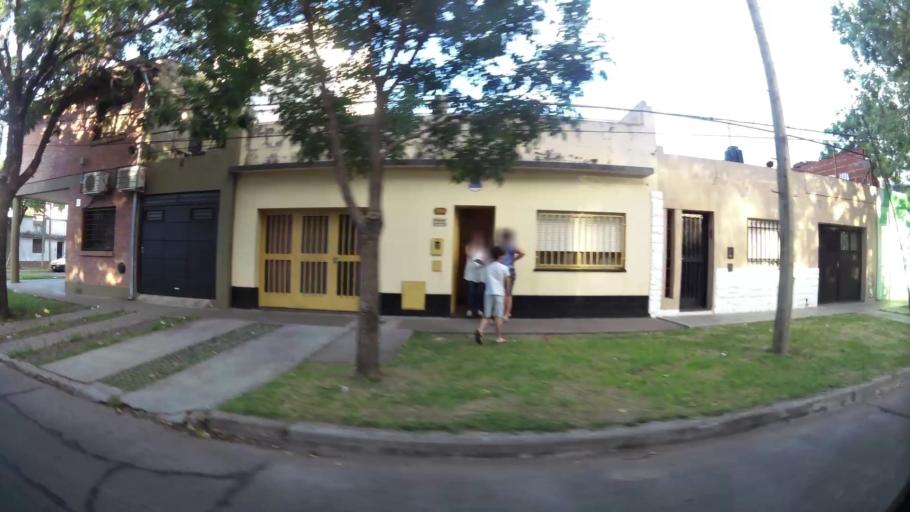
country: AR
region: Santa Fe
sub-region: Departamento de Rosario
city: Rosario
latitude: -32.9705
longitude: -60.6628
